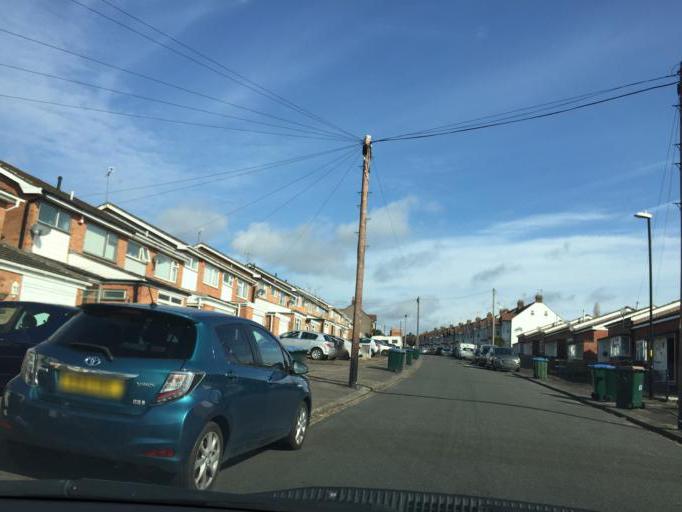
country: GB
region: England
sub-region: Coventry
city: Coventry
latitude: 52.3902
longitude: -1.4963
